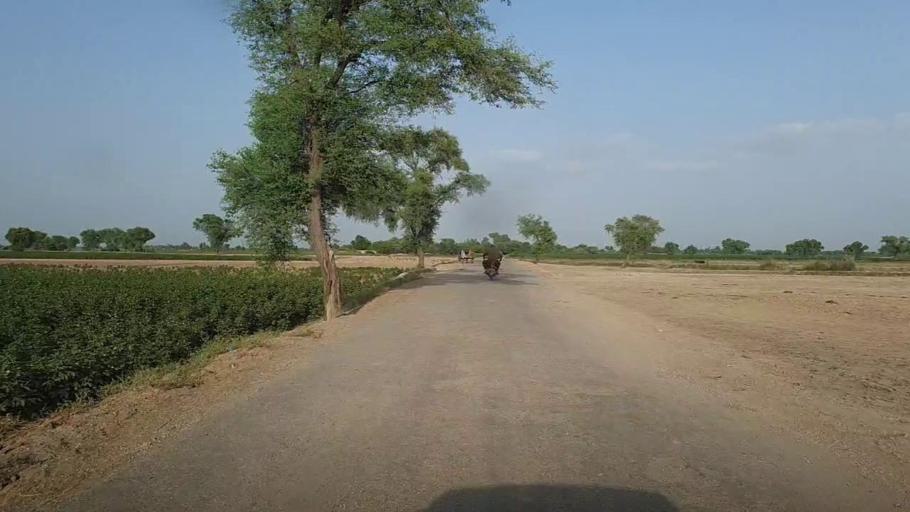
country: PK
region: Sindh
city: Khairpur
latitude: 28.0829
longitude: 69.7958
